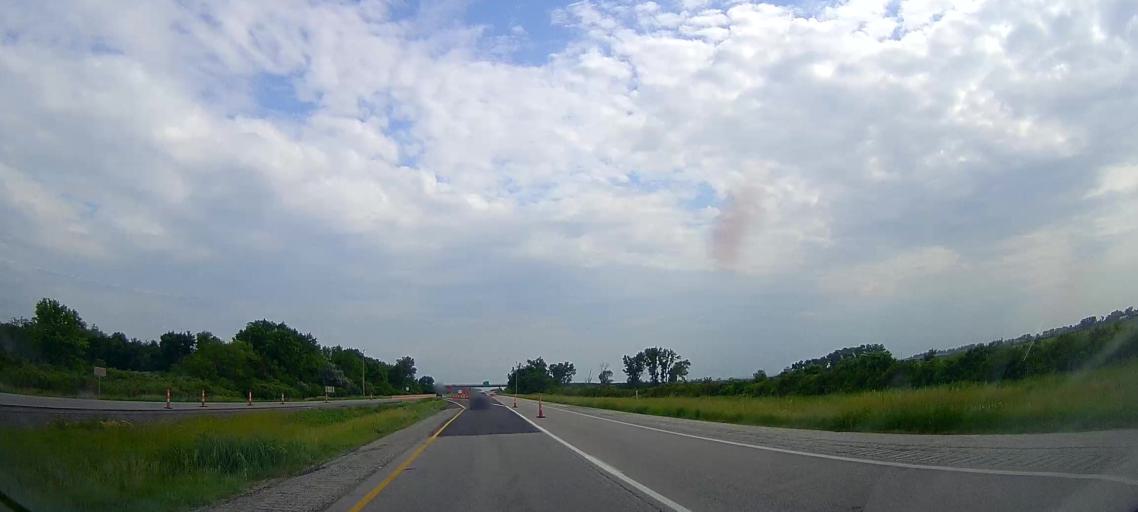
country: US
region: Nebraska
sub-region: Burt County
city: Tekamah
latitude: 41.7332
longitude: -96.0481
